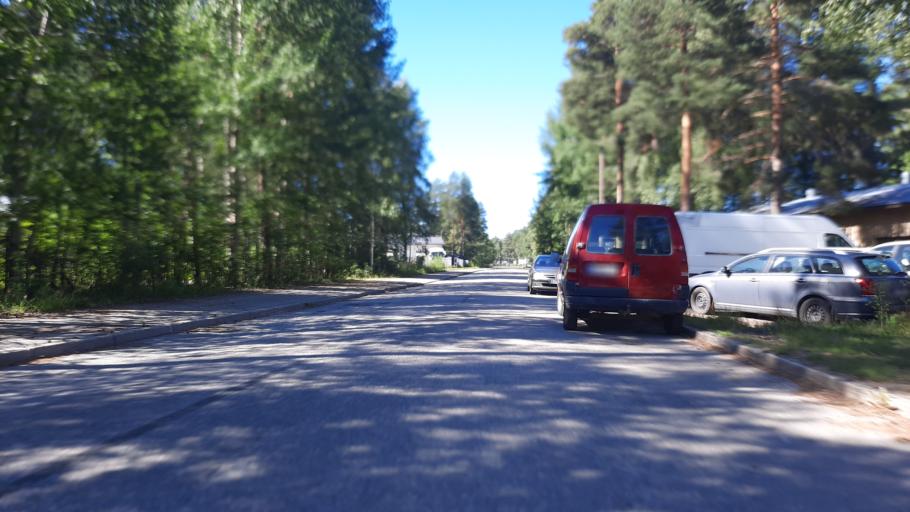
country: FI
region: North Karelia
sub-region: Joensuu
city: Joensuu
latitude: 62.6238
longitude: 29.7482
